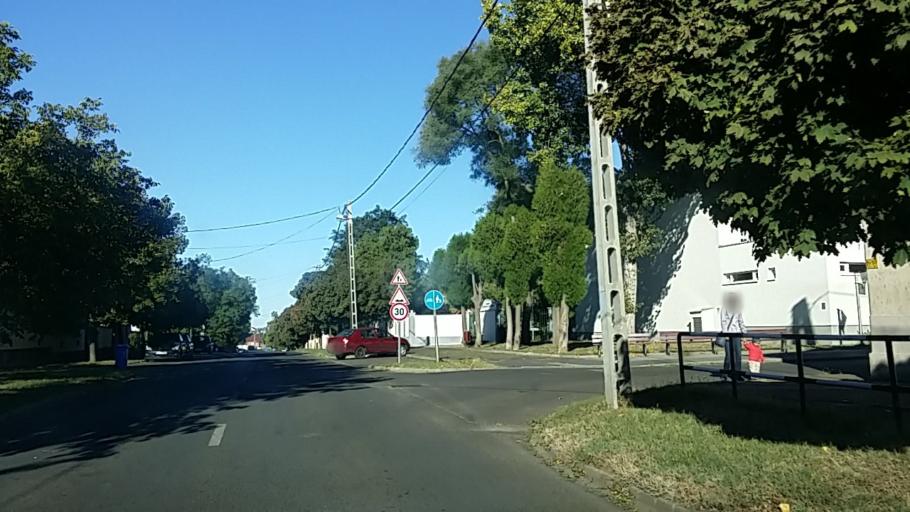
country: HU
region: Heves
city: Gyongyos
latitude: 47.7889
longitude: 19.9353
